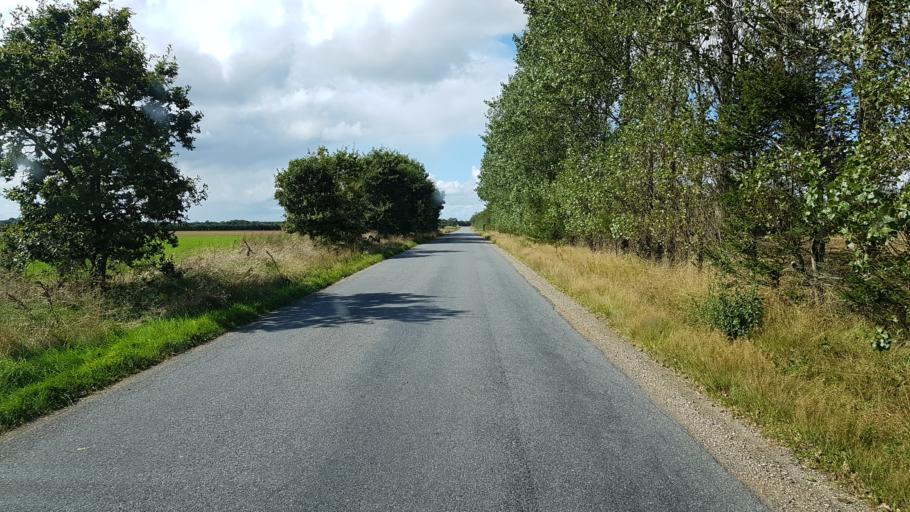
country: DK
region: South Denmark
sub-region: Esbjerg Kommune
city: Bramming
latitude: 55.6152
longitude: 8.7496
